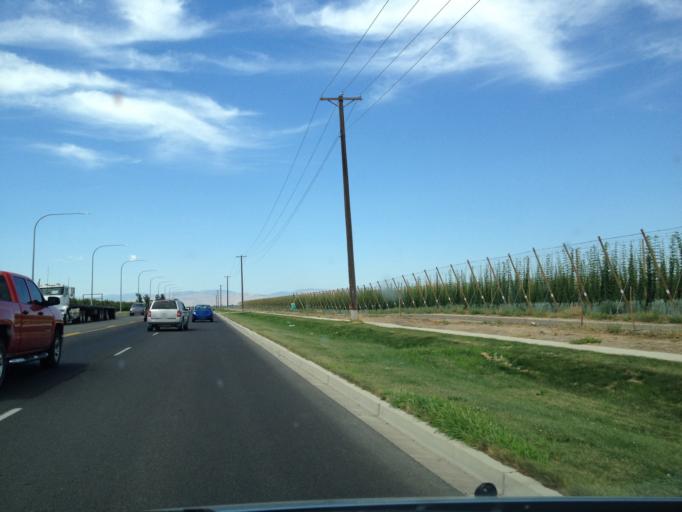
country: US
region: Washington
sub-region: Yakima County
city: West Valley
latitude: 46.5857
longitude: -120.5840
